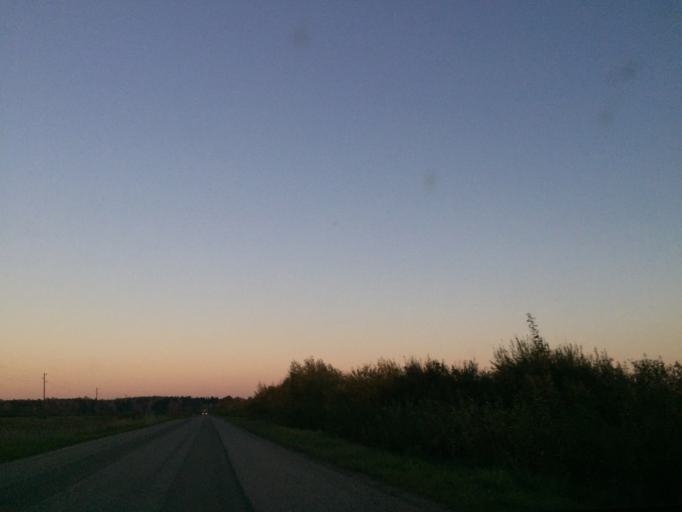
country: LT
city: Vieksniai
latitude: 56.4003
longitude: 22.5414
